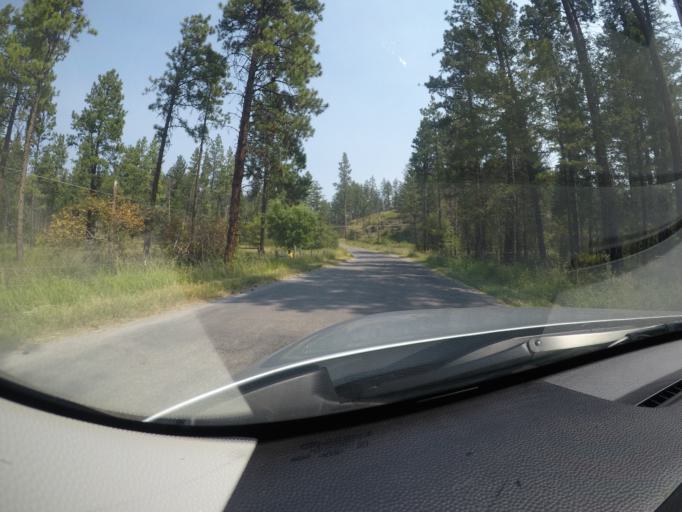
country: US
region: Montana
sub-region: Lake County
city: Polson
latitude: 47.7720
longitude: -114.1458
